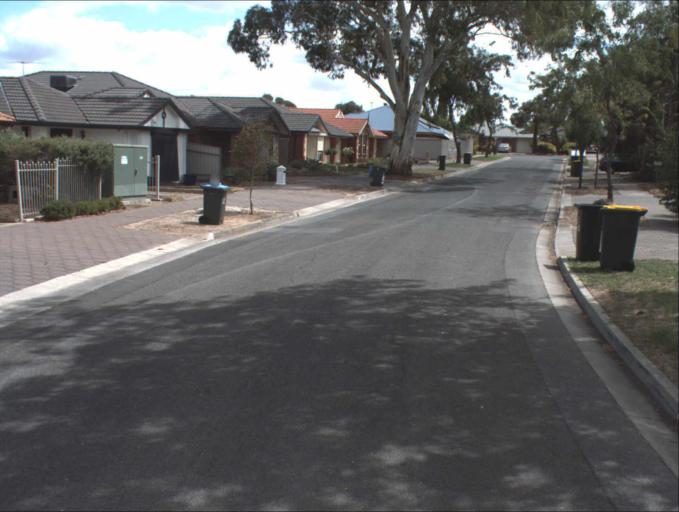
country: AU
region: South Australia
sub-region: Port Adelaide Enfield
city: Gilles Plains
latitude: -34.8596
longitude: 138.6605
